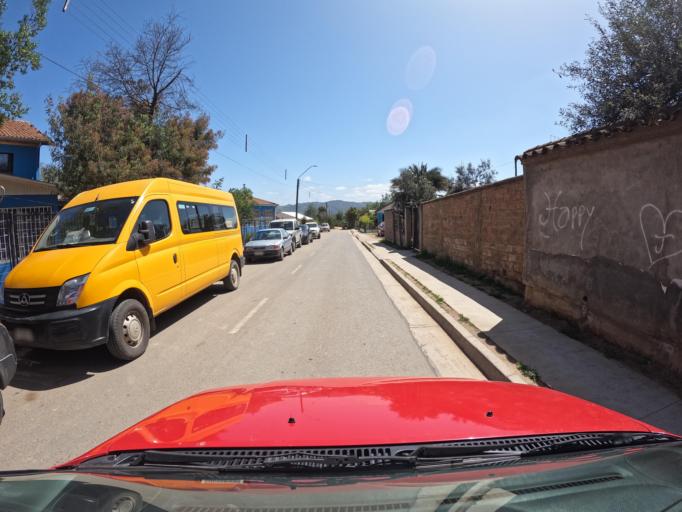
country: CL
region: O'Higgins
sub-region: Provincia de Colchagua
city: Santa Cruz
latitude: -34.7284
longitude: -71.6457
